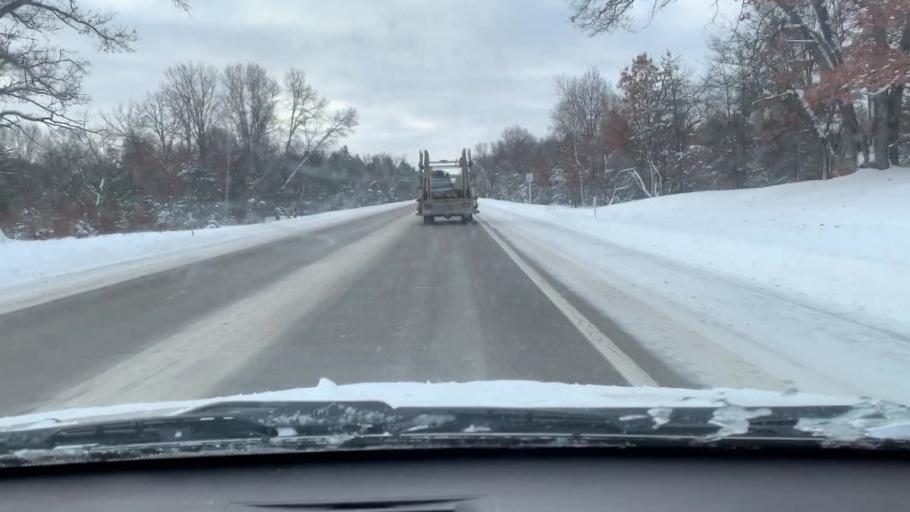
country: US
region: Michigan
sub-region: Wexford County
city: Manton
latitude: 44.5023
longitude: -85.4059
